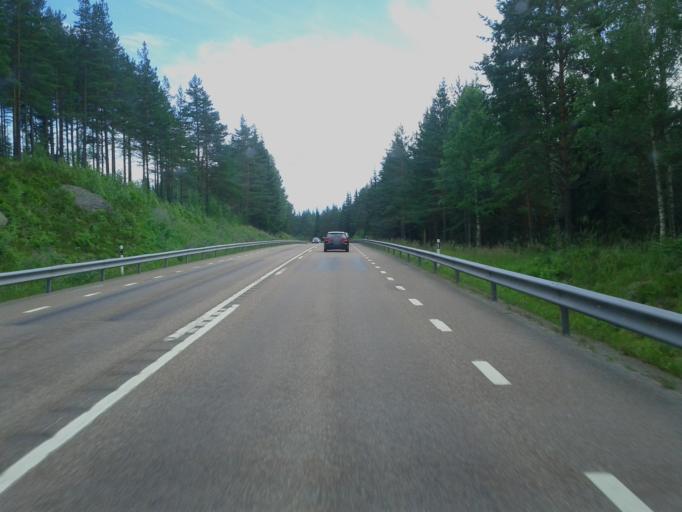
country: SE
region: Dalarna
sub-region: Faluns Kommun
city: Grycksbo
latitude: 60.7089
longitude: 15.4638
